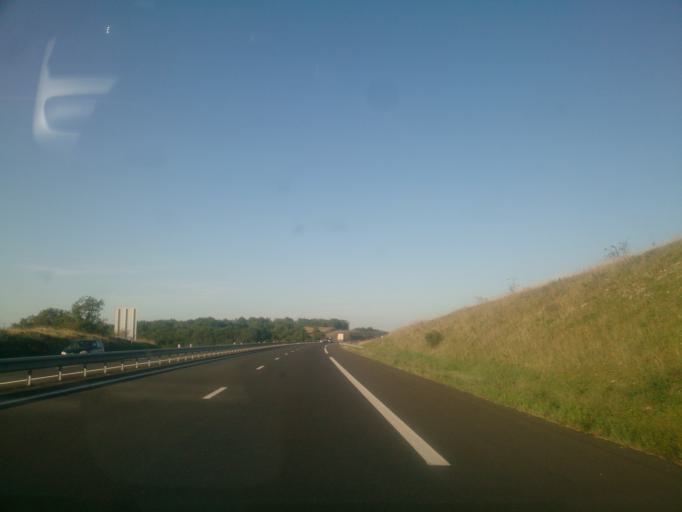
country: FR
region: Midi-Pyrenees
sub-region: Departement du Lot
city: Le Vigan
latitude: 44.6325
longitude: 1.5229
